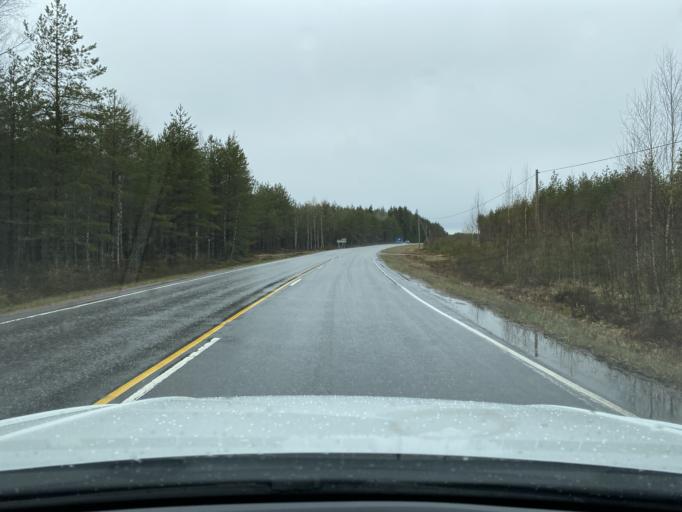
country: FI
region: Satakunta
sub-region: Pori
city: Vampula
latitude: 60.9509
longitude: 22.6762
